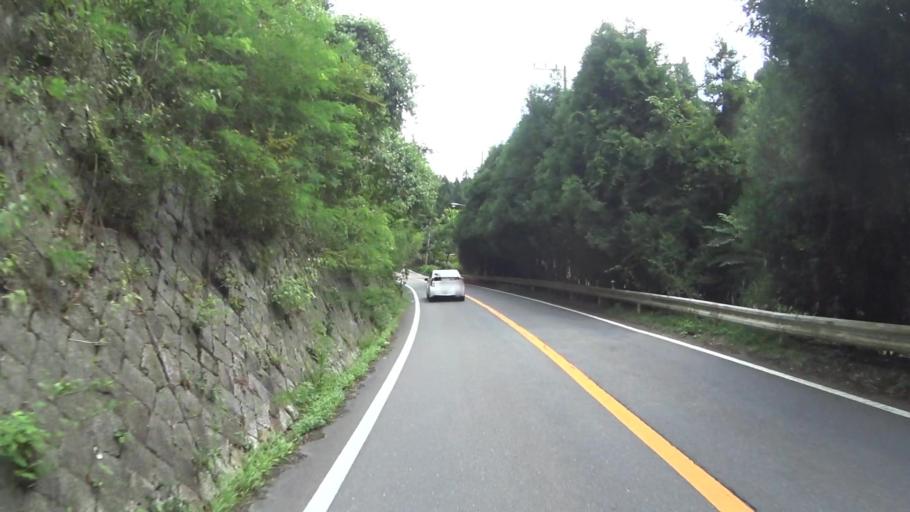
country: JP
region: Kyoto
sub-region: Kyoto-shi
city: Kamigyo-ku
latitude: 35.1105
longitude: 135.8060
